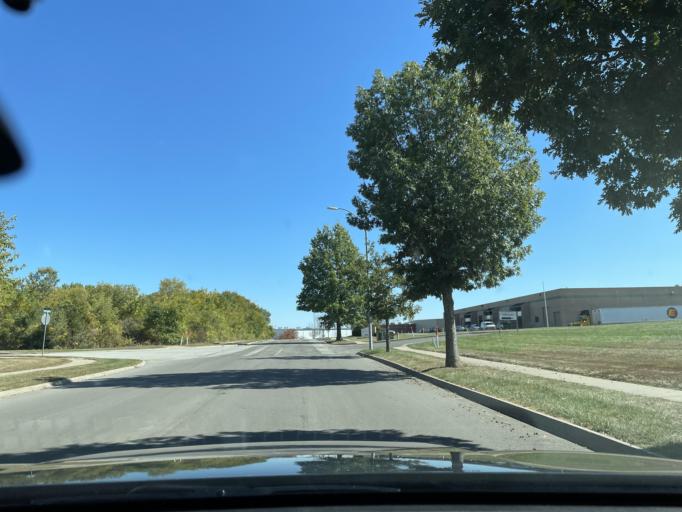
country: US
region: Missouri
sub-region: Buchanan County
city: Saint Joseph
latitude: 39.7508
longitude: -94.7611
